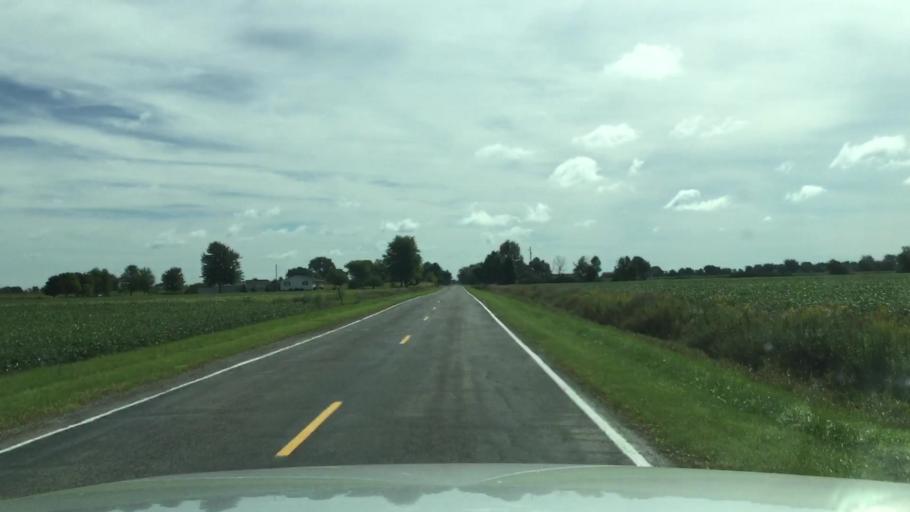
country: US
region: Michigan
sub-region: Saginaw County
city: Chesaning
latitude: 43.1465
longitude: -84.0067
